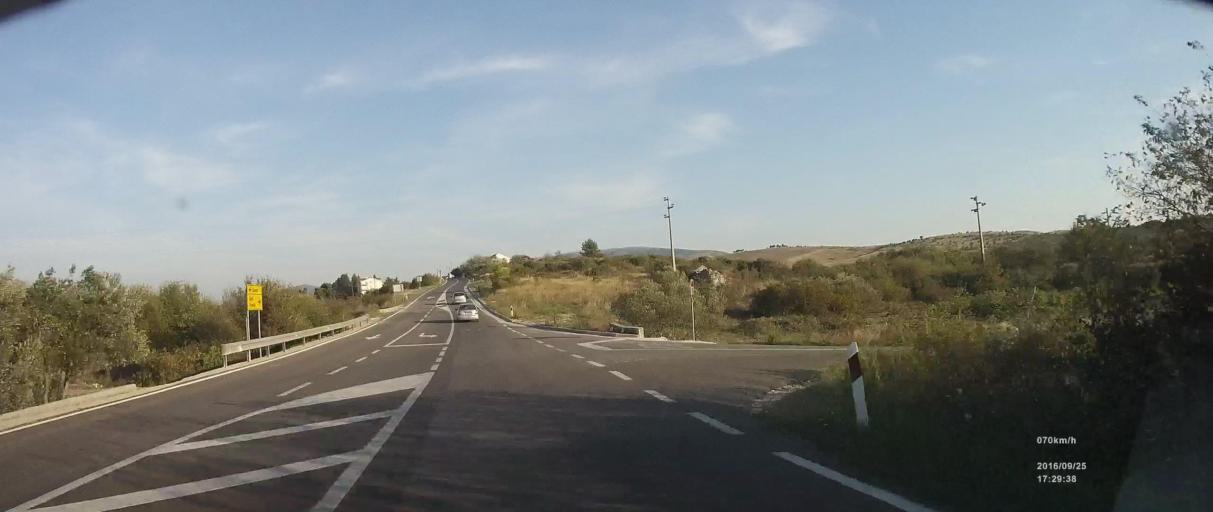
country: HR
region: Sibensko-Kniniska
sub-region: Grad Sibenik
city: Brodarica
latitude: 43.6851
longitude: 15.9676
